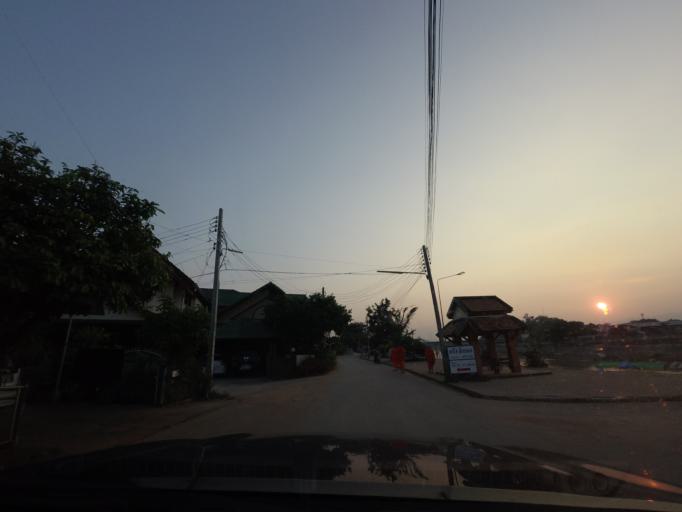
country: TH
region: Nan
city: Nan
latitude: 18.7768
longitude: 100.7828
